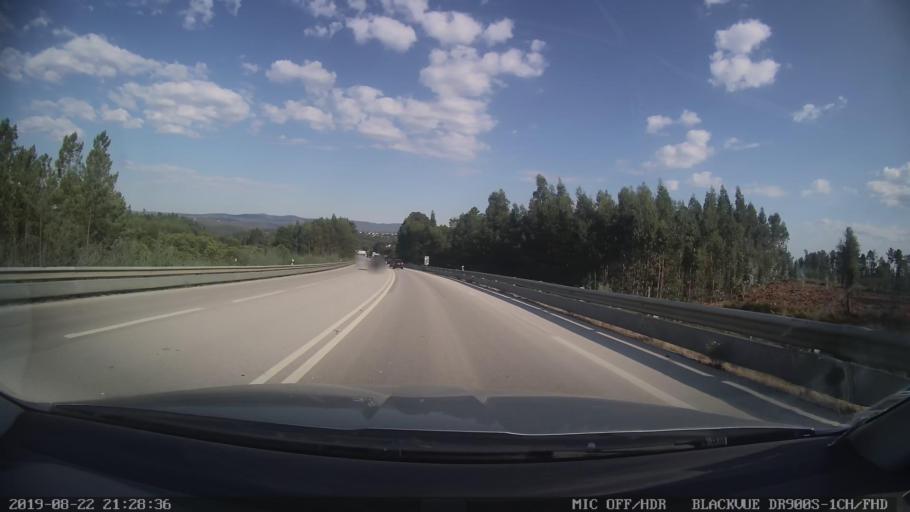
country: PT
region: Leiria
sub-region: Pedrogao Grande
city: Pedrogao Grande
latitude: 39.8948
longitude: -8.1224
